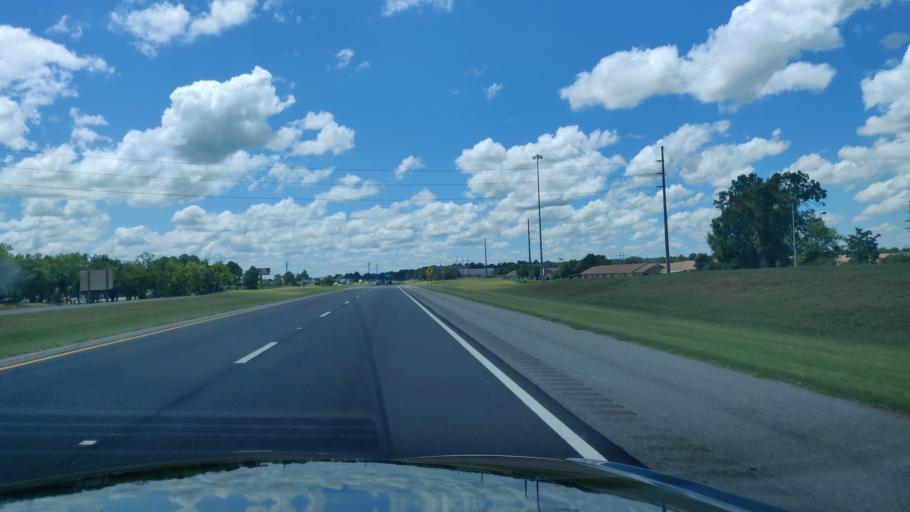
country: US
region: Georgia
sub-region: Dougherty County
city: Albany
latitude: 31.6182
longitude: -84.2066
